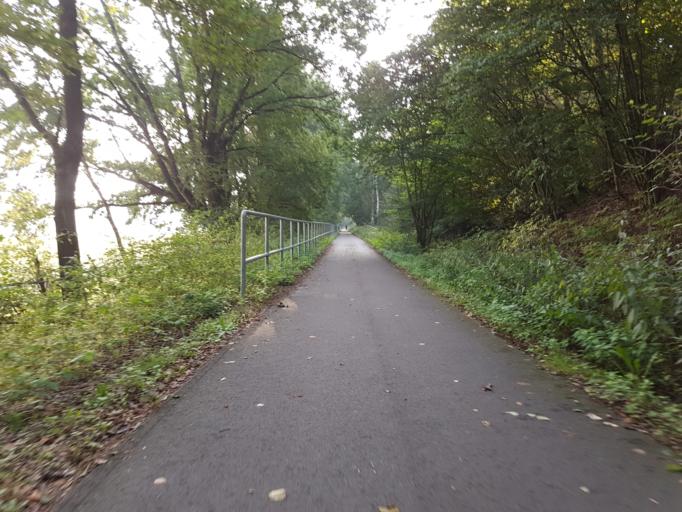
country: DE
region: Saxony
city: Claussnitz
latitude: 50.9143
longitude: 12.8904
